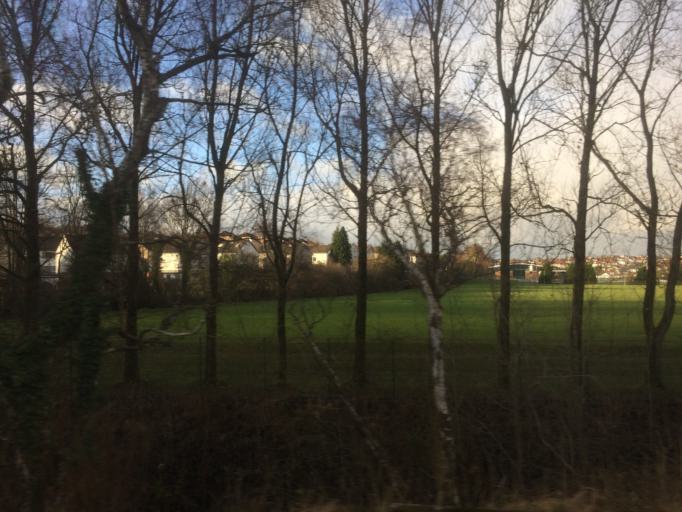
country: GB
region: Scotland
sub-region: East Renfrewshire
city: Giffnock
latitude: 55.8059
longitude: -4.2765
